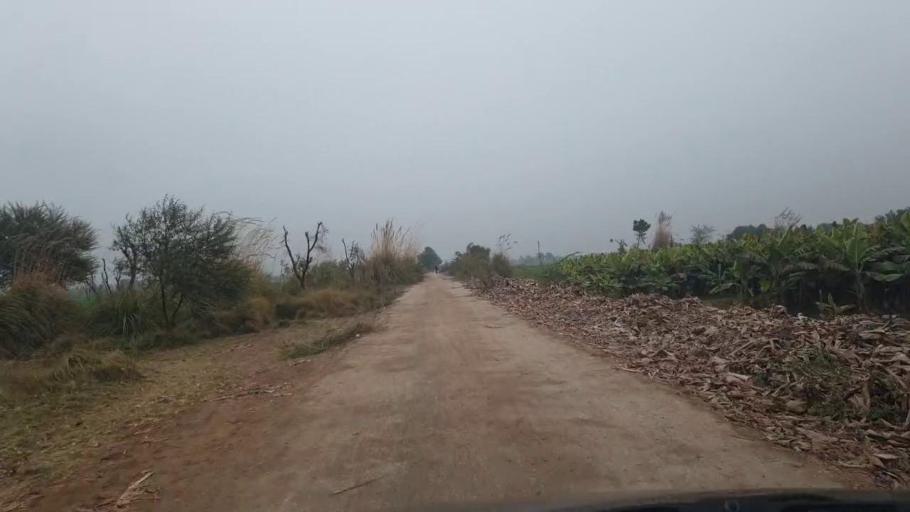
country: PK
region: Sindh
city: Tando Adam
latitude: 25.8468
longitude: 68.7025
